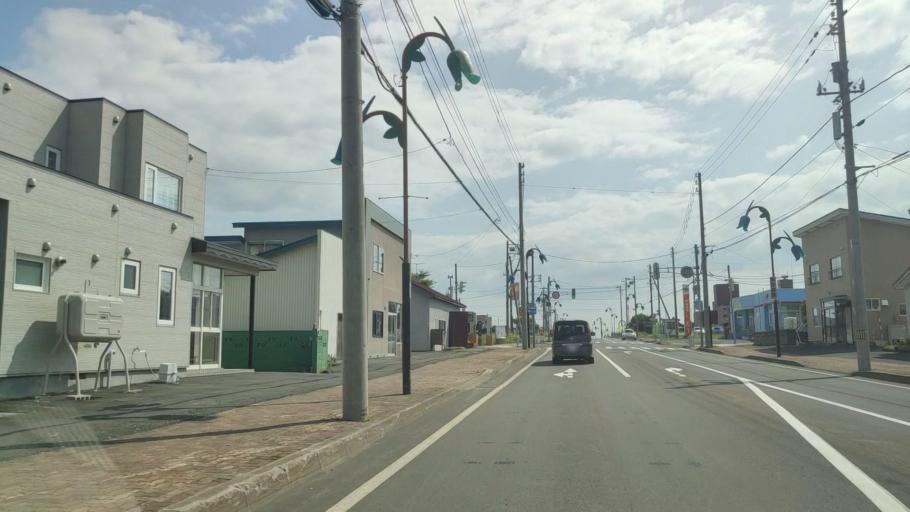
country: JP
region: Hokkaido
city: Rumoi
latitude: 44.3081
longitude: 141.6540
